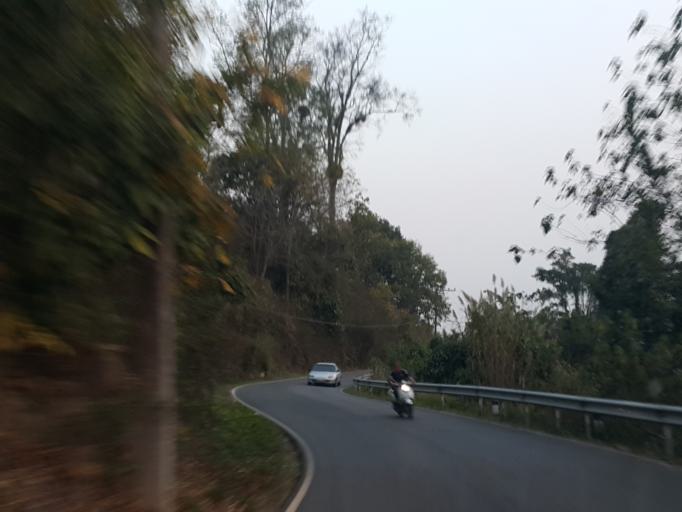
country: TH
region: Chiang Mai
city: Mae Taeng
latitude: 18.9995
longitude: 98.8885
